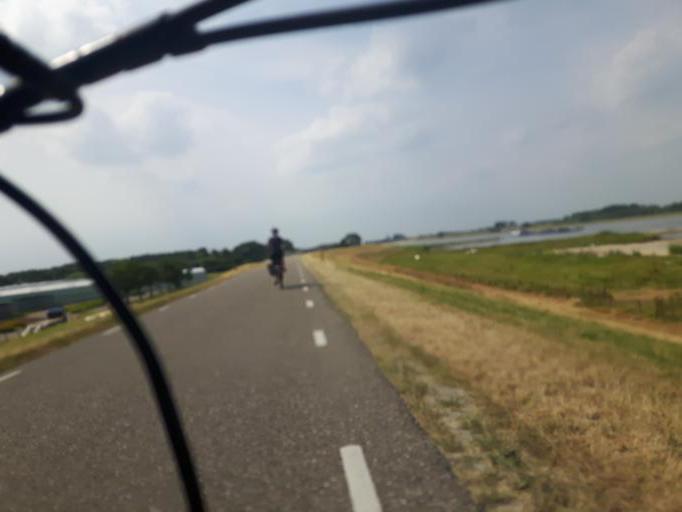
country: NL
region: Gelderland
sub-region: Gemeente Zaltbommel
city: Nederhemert-Noord
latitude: 51.8096
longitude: 5.1895
